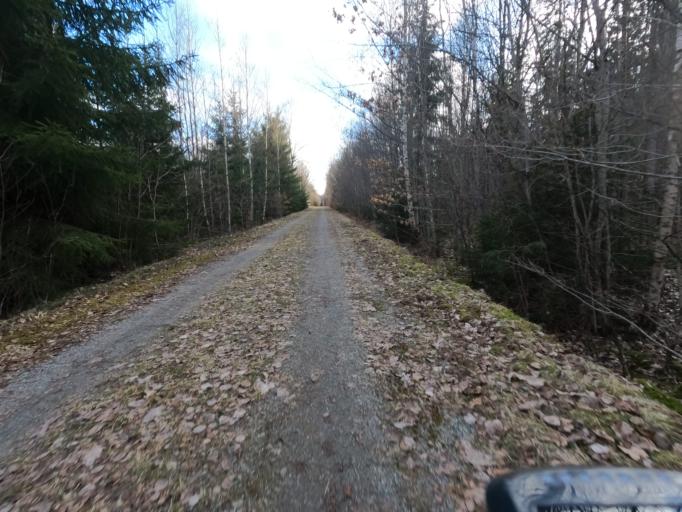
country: SE
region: Kronoberg
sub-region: Alvesta Kommun
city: Vislanda
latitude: 56.6429
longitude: 14.6166
